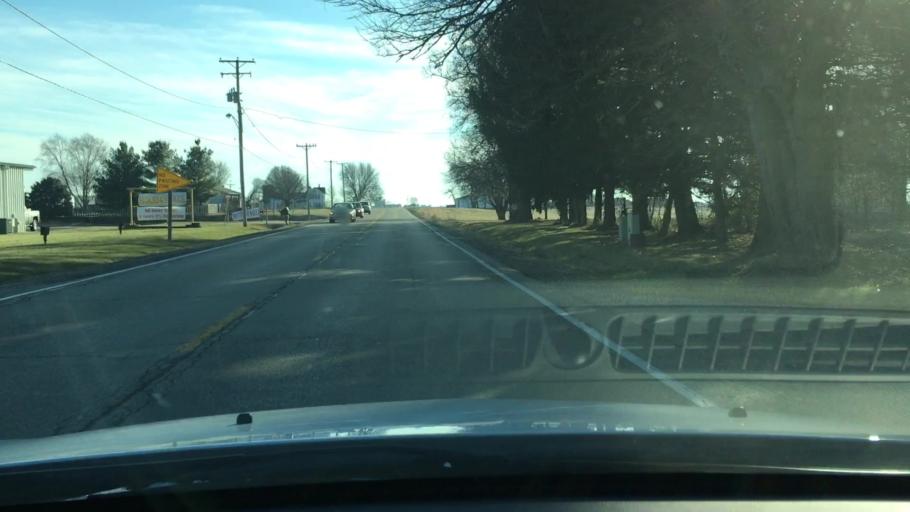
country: US
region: Illinois
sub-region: LaSalle County
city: Mendota
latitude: 41.5195
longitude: -89.1274
